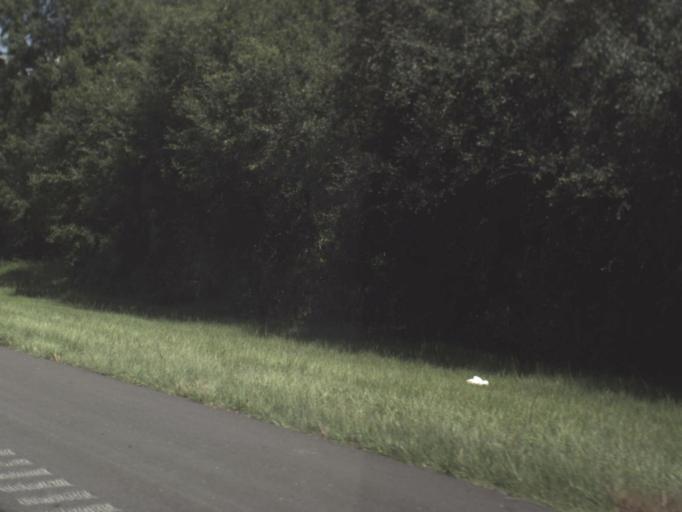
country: US
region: Florida
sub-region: Madison County
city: Madison
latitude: 30.4048
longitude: -83.3960
